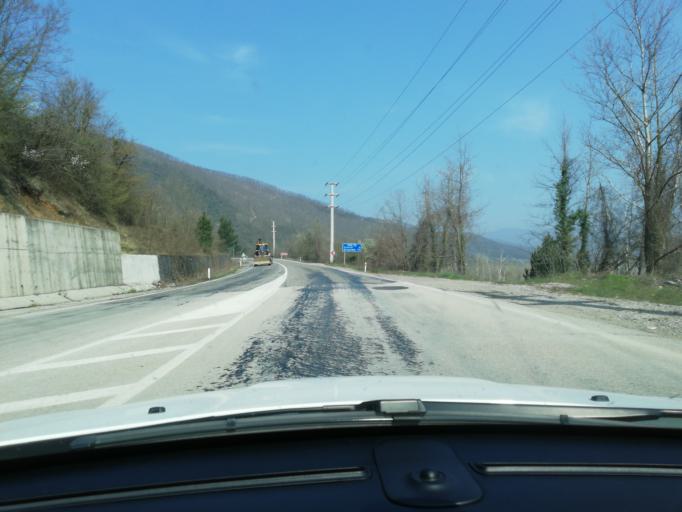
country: TR
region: Karabuk
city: Yenice
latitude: 41.2075
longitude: 32.3642
